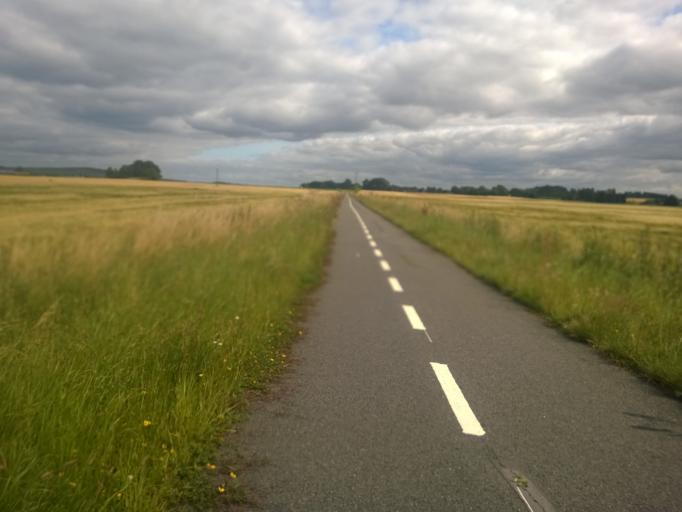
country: SE
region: Skane
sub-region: Kristianstads Kommun
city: Kristianstad
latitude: 56.0653
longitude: 14.1899
